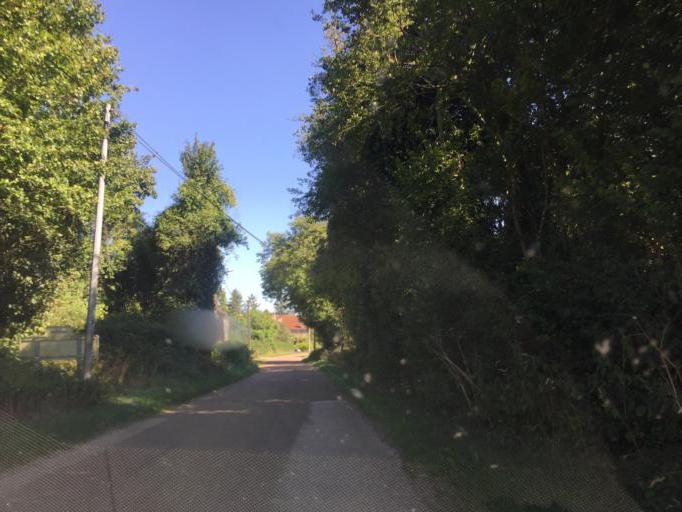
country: FR
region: Bourgogne
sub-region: Departement de l'Yonne
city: Fontenailles
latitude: 47.5283
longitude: 3.3456
